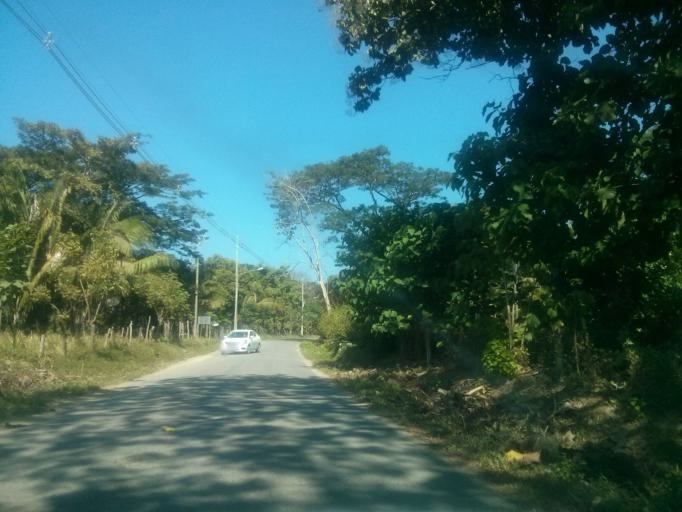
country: CR
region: Puntarenas
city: Paquera
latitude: 9.6236
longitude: -85.1466
